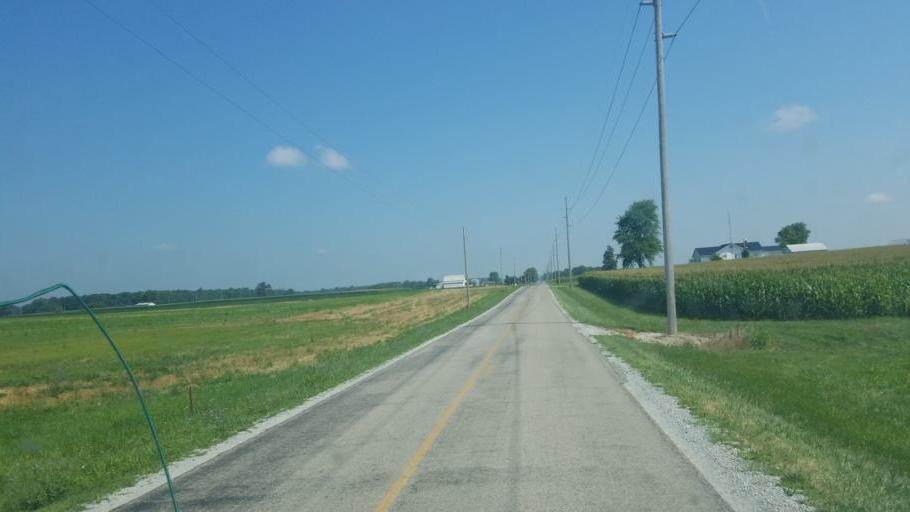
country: US
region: Ohio
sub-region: Hardin County
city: Kenton
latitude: 40.6810
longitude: -83.6543
